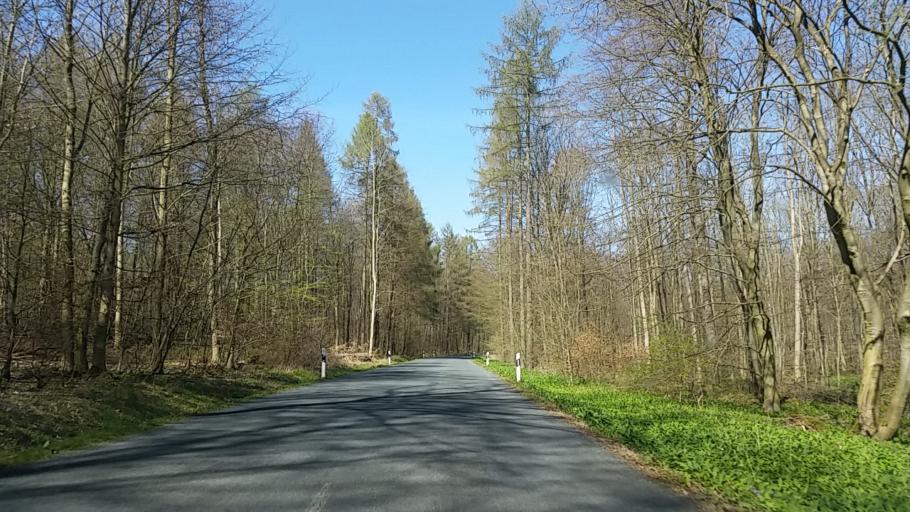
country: DE
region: Lower Saxony
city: Kneitlingen
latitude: 52.1988
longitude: 10.7598
